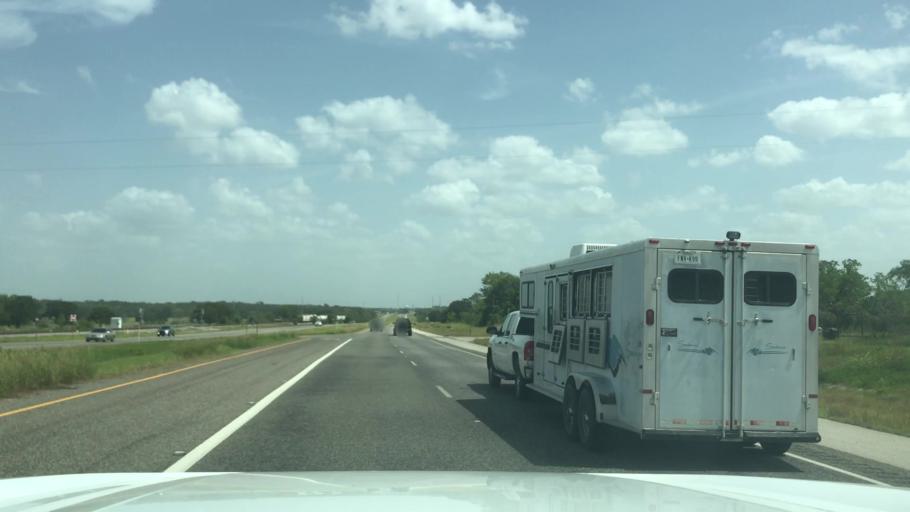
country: US
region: Texas
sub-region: Robertson County
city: Hearne
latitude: 30.9229
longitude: -96.6252
